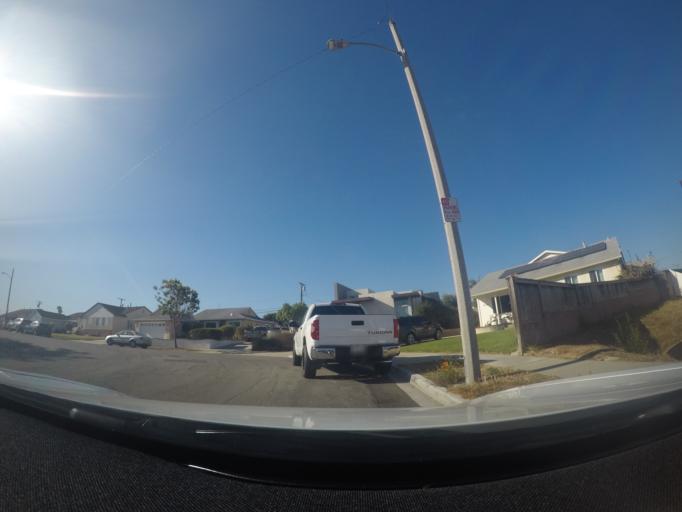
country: US
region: California
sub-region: Los Angeles County
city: Torrance
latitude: 33.8530
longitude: -118.3569
